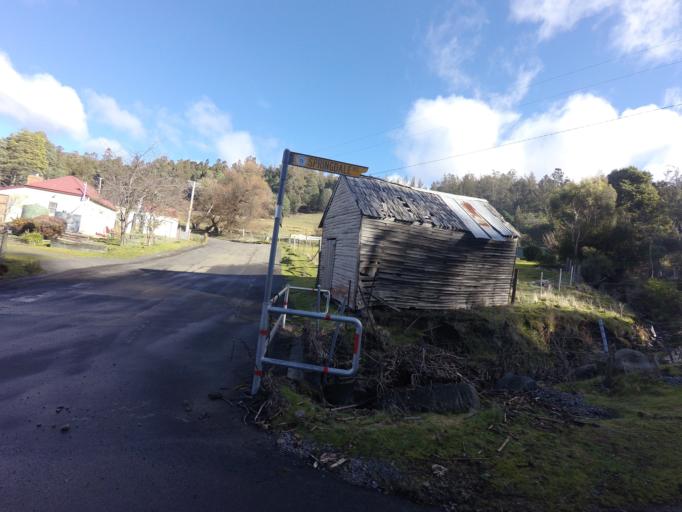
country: AU
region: Tasmania
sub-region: Glenorchy
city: Berriedale
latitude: -42.8504
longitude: 147.1686
